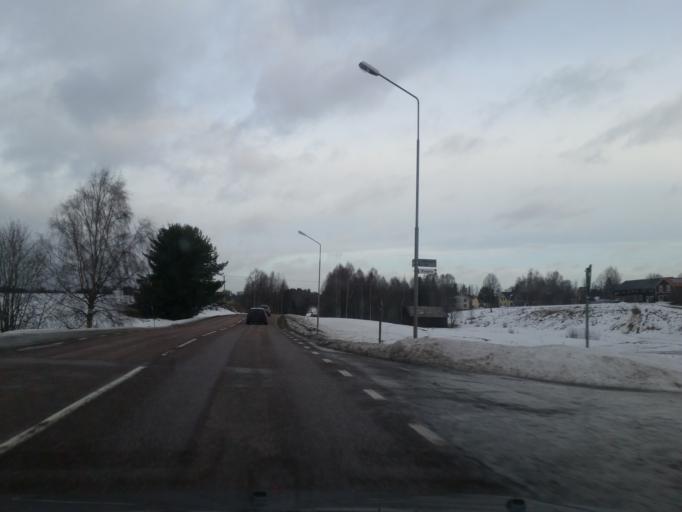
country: SE
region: Gaevleborg
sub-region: Sandvikens Kommun
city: Jarbo
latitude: 60.7016
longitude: 16.6127
